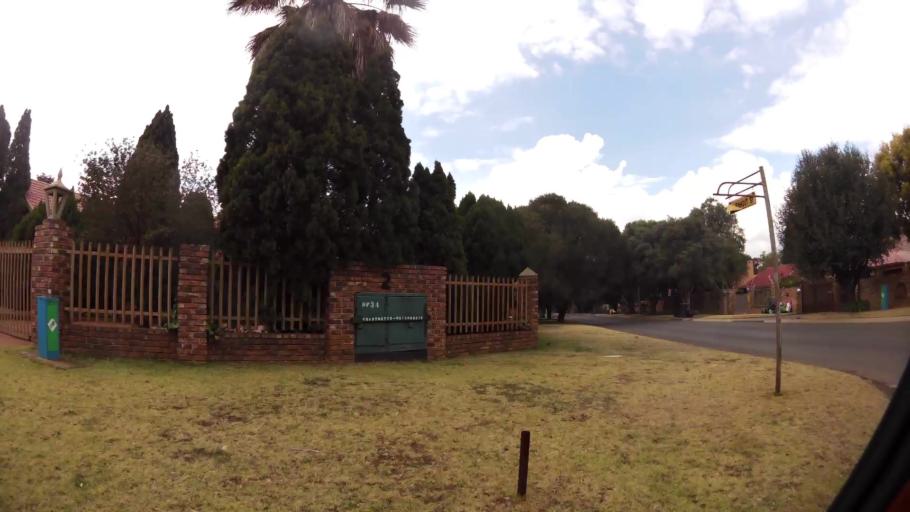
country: ZA
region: Gauteng
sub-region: Sedibeng District Municipality
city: Vanderbijlpark
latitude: -26.7358
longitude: 27.8503
